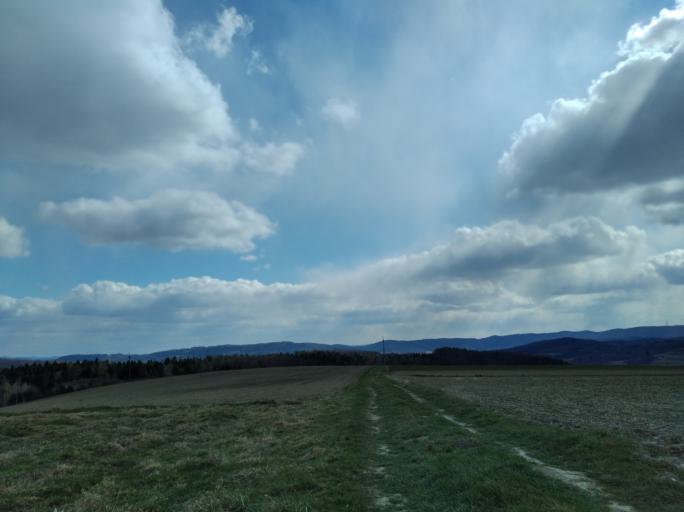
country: PL
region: Subcarpathian Voivodeship
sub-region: Powiat strzyzowski
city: Jawornik
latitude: 49.8401
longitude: 21.8538
